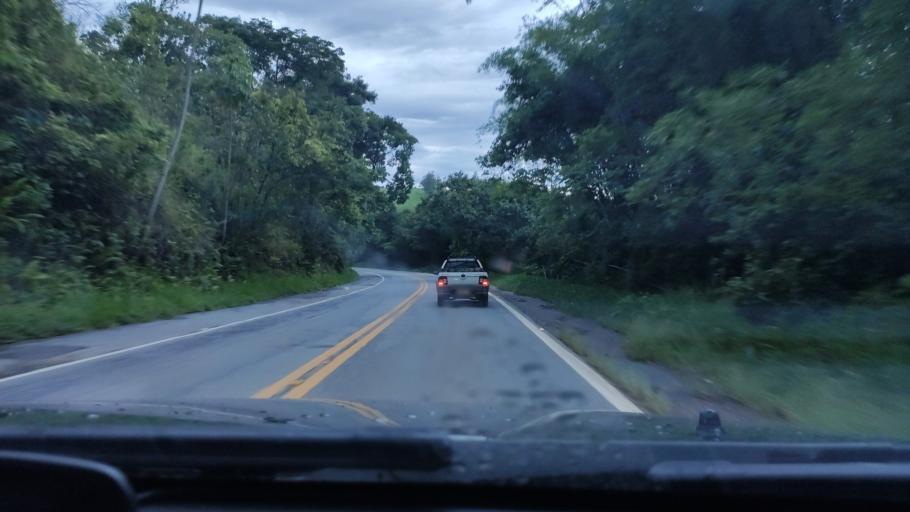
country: BR
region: Sao Paulo
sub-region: Socorro
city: Socorro
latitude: -22.6622
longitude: -46.5467
